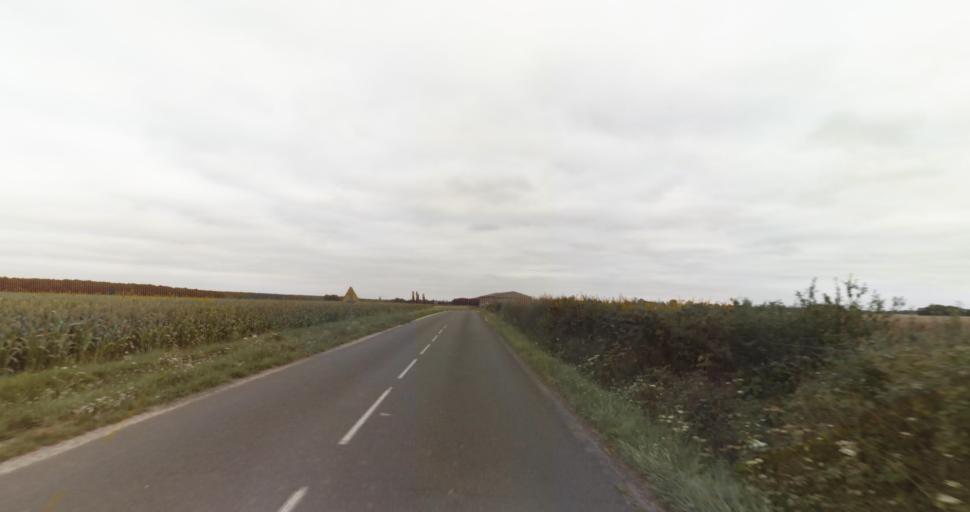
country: FR
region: Haute-Normandie
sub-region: Departement de l'Eure
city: Marcilly-sur-Eure
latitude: 48.9015
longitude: 1.2813
